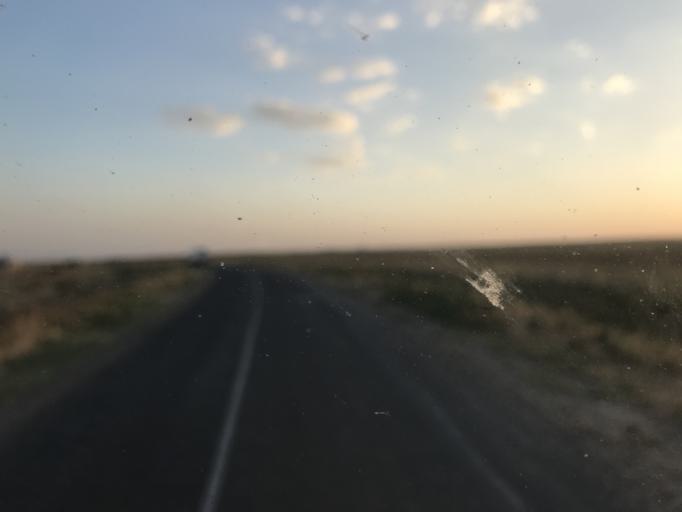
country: UZ
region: Toshkent
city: Yangiyul
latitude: 41.3831
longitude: 68.7622
